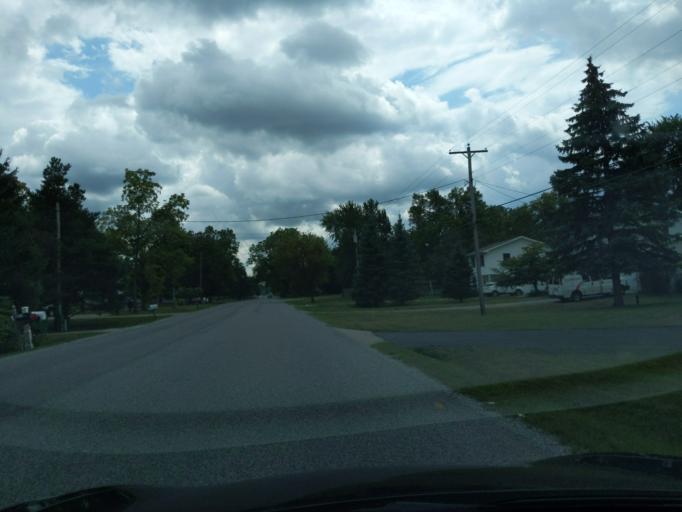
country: US
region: Michigan
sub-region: Eaton County
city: Dimondale
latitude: 42.6585
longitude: -84.5826
